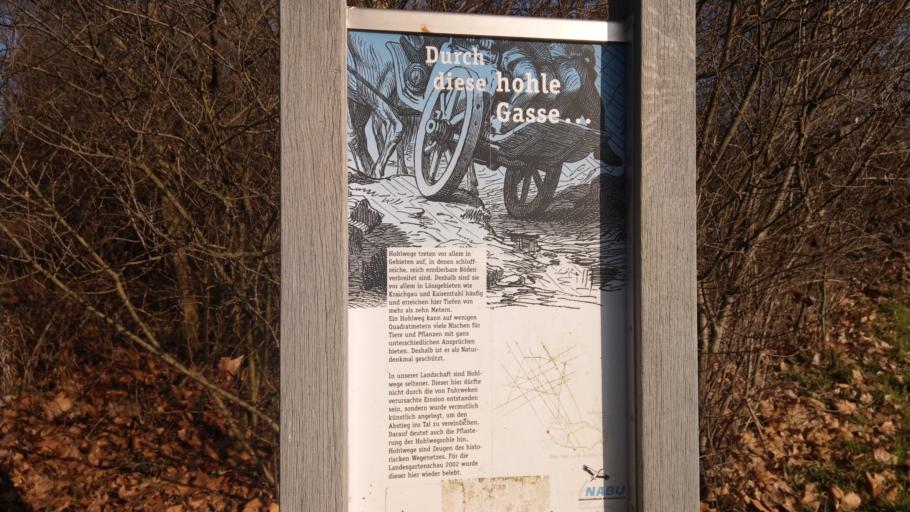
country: DE
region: Baden-Wuerttemberg
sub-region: Regierungsbezirk Stuttgart
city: Ostfildern
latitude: 48.7118
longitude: 9.2618
